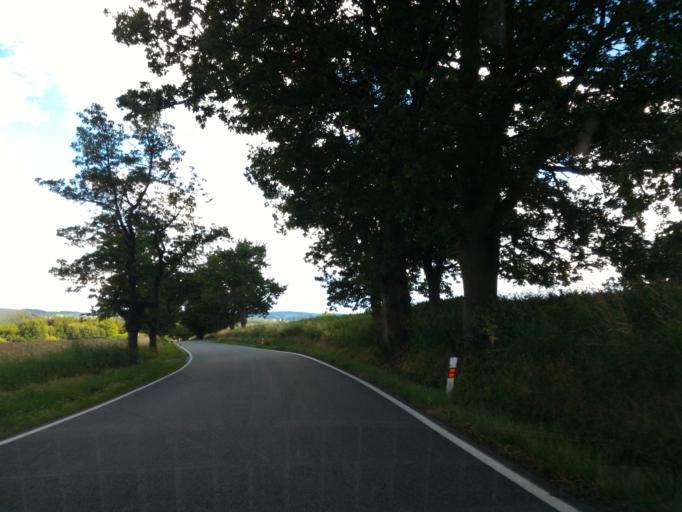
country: CZ
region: Vysocina
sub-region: Okres Jihlava
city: Telc
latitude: 49.2184
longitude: 15.4235
